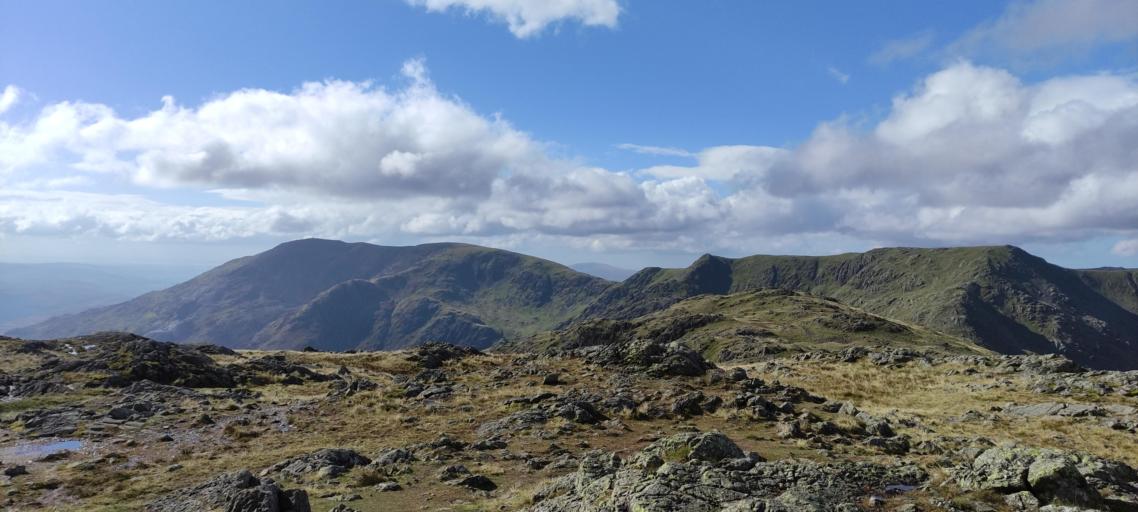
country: GB
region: England
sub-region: Cumbria
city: Ambleside
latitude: 54.4004
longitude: -3.0980
